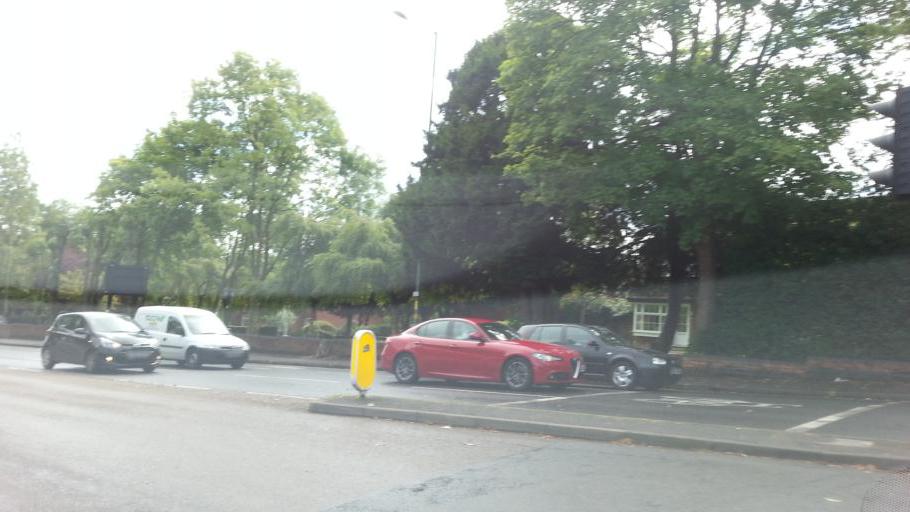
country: GB
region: England
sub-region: City and Borough of Birmingham
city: Birmingham
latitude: 52.4558
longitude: -1.9099
